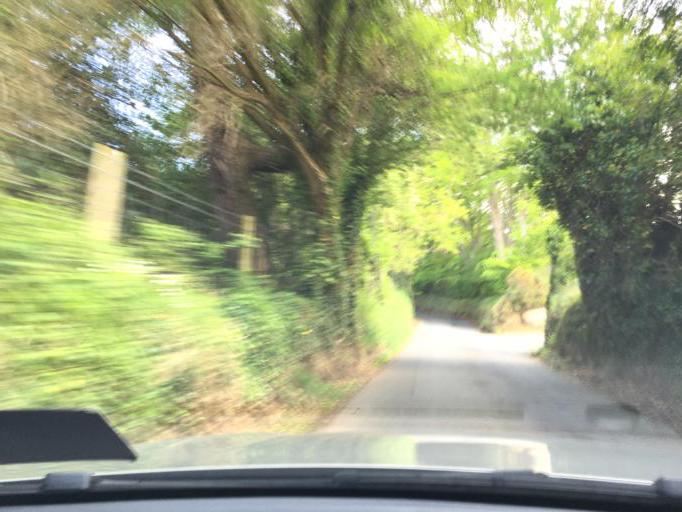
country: IE
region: Leinster
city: Ballinteer
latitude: 53.2598
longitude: -6.2774
